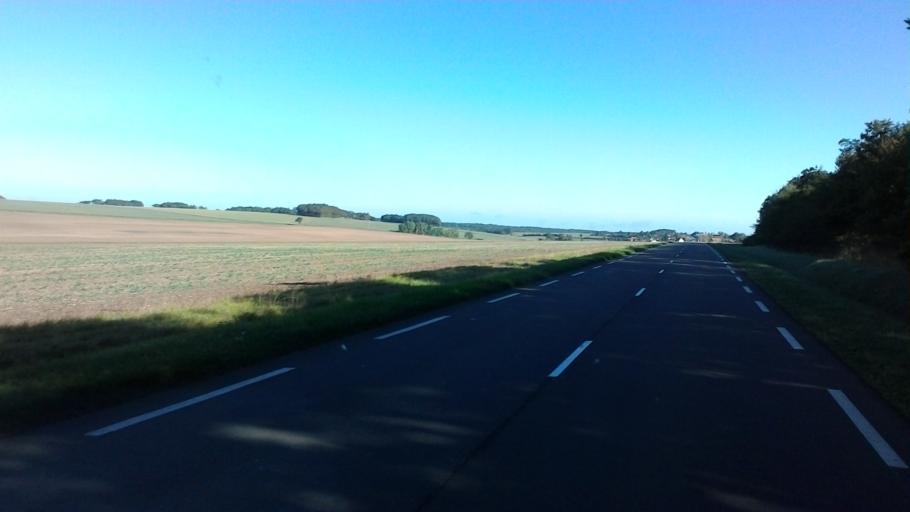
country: FR
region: Bourgogne
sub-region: Departement de la Cote-d'Or
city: Chatillon-sur-Seine
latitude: 47.7982
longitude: 4.5209
